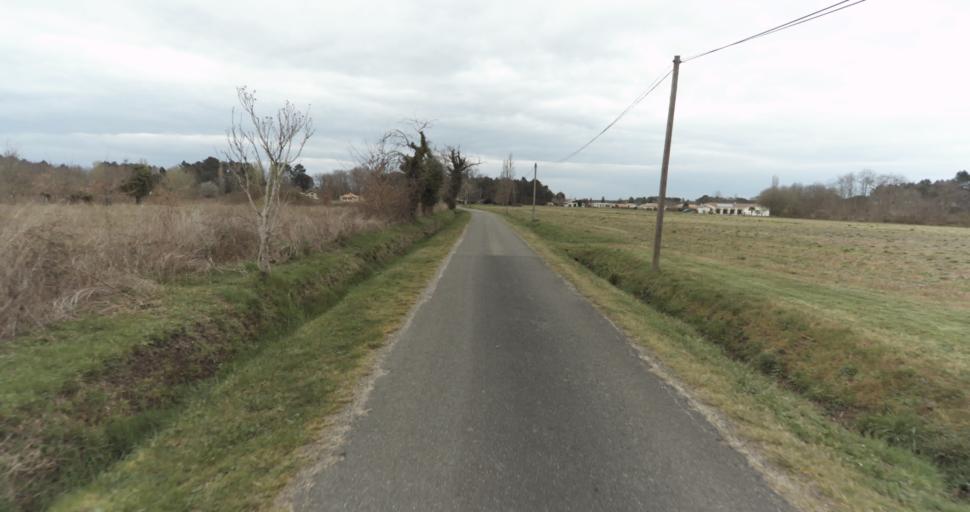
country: FR
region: Aquitaine
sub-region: Departement des Landes
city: Sarbazan
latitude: 44.0164
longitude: -0.3190
